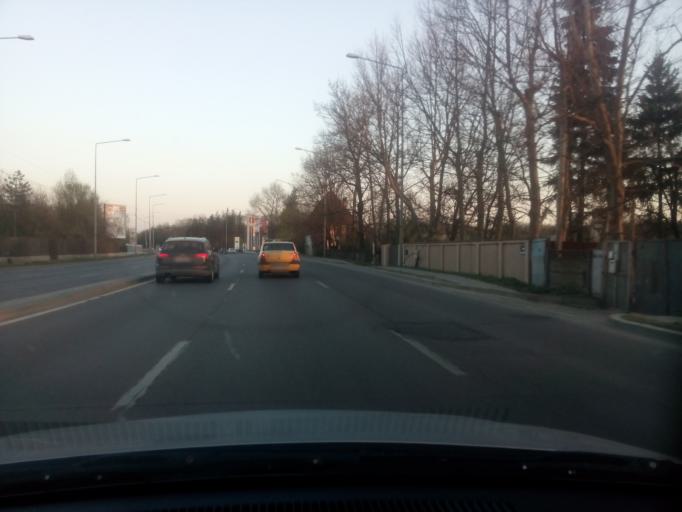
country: RO
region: Ilfov
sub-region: Comuna Otopeni
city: Otopeni
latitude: 44.5266
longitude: 26.0711
